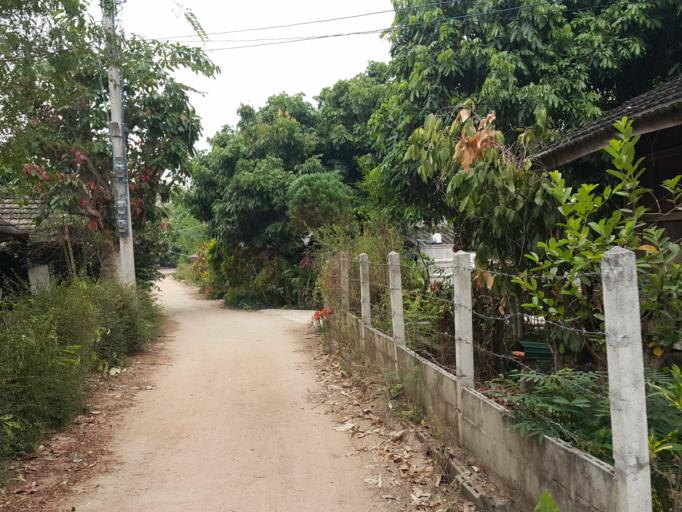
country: TH
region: Chiang Mai
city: Mae Taeng
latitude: 19.1050
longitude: 98.9946
